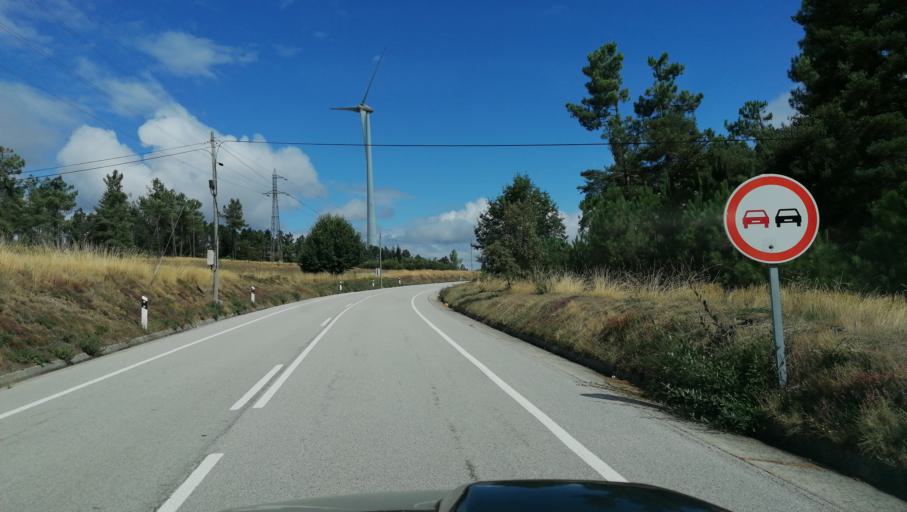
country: PT
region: Vila Real
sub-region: Vila Pouca de Aguiar
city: Vila Pouca de Aguiar
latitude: 41.5229
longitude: -7.5937
